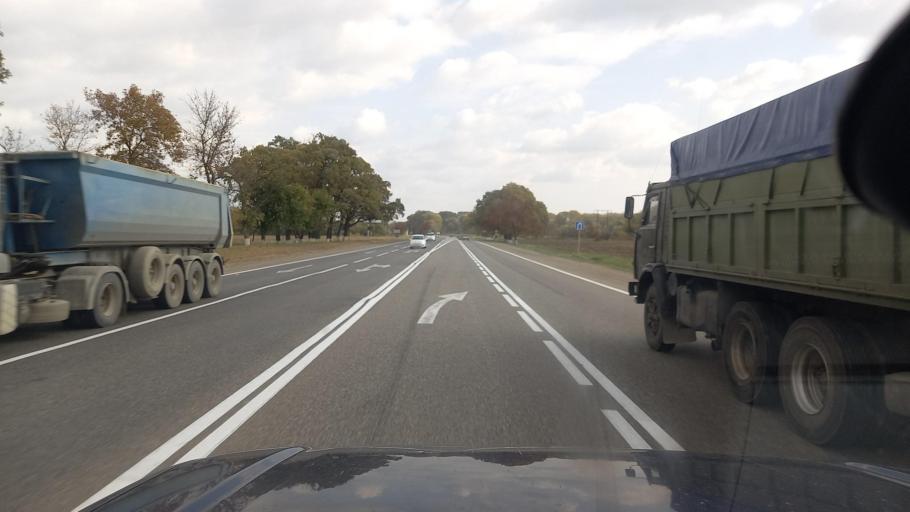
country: RU
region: Krasnodarskiy
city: Chernomorskiy
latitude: 44.8516
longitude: 38.4418
